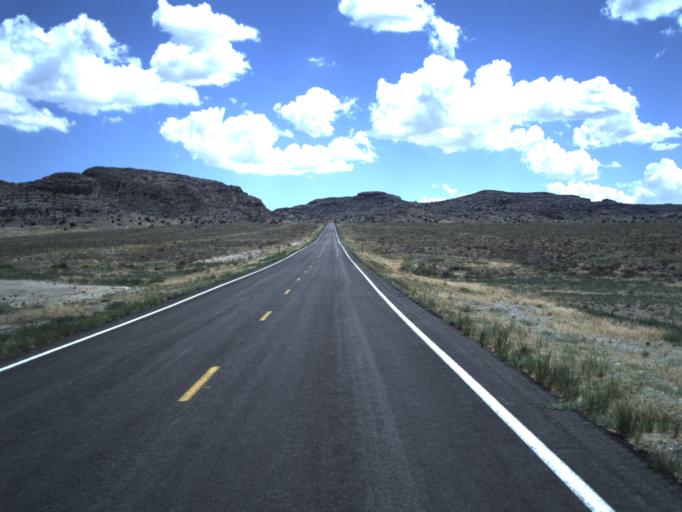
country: US
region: Utah
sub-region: Beaver County
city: Milford
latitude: 39.0753
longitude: -113.6779
